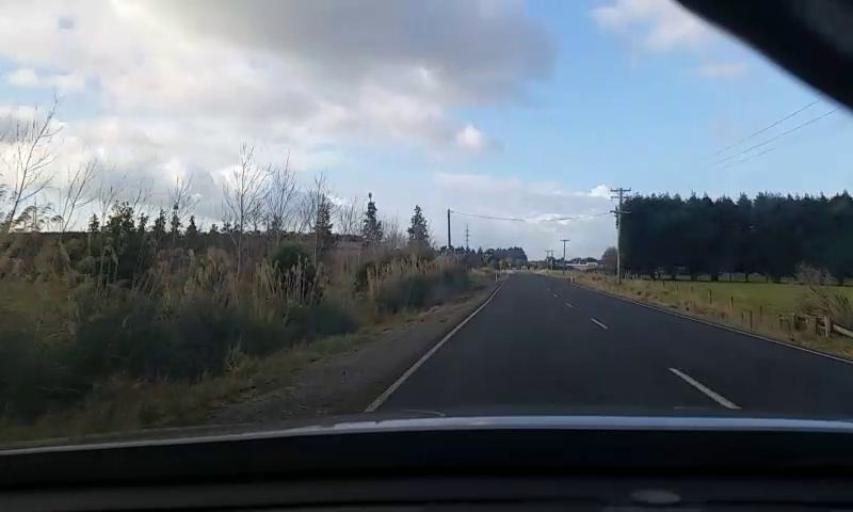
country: NZ
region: Southland
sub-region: Invercargill City
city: Invercargill
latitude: -46.3815
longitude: 168.4494
